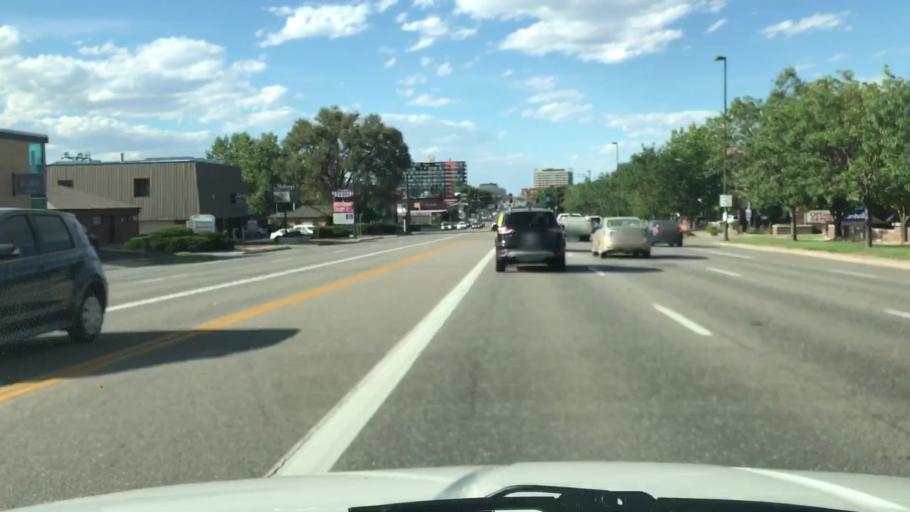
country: US
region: Colorado
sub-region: Arapahoe County
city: Cherry Hills Village
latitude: 39.6660
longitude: -104.9406
